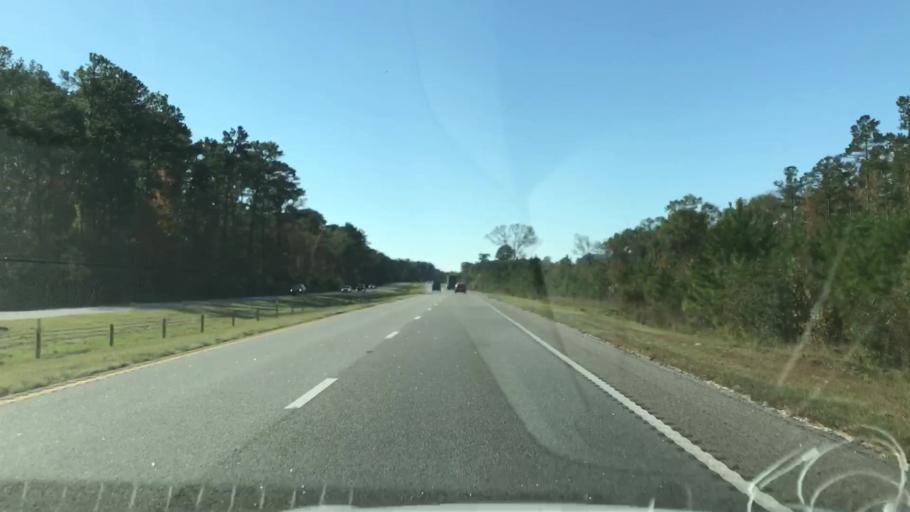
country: US
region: South Carolina
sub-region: Colleton County
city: Walterboro
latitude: 32.7221
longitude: -80.6024
